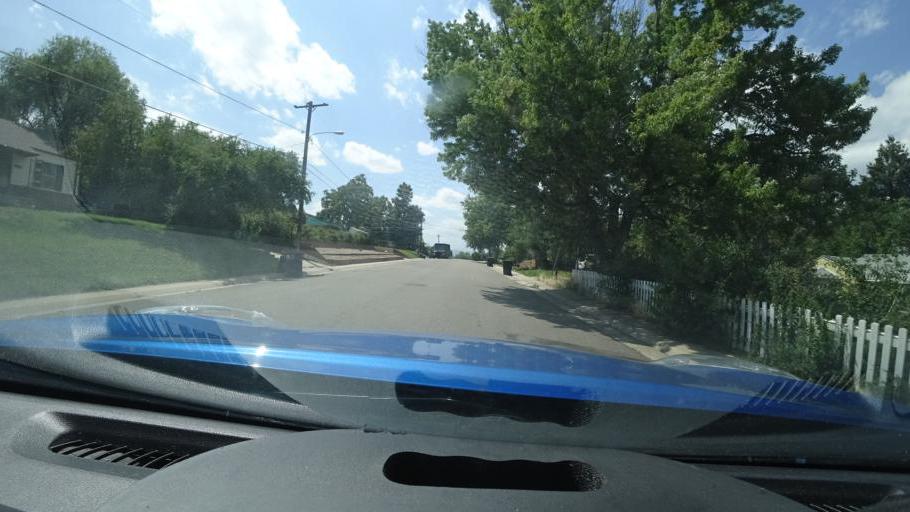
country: US
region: Colorado
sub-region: Arapahoe County
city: Sheridan
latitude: 39.6850
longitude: -105.0281
